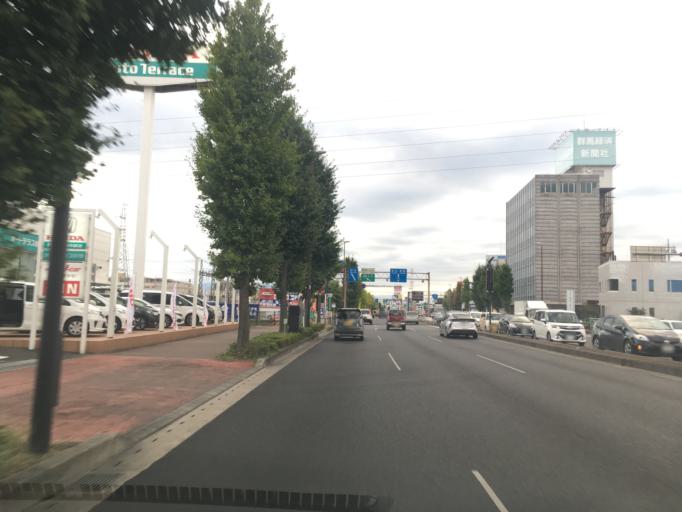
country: JP
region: Gunma
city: Maebashi-shi
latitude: 36.3790
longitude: 139.0377
